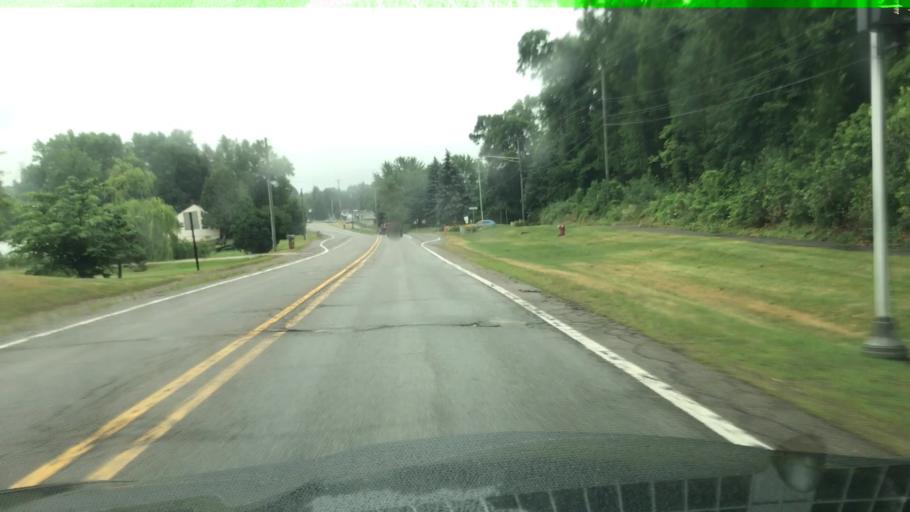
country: US
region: Michigan
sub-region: Oakland County
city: Auburn Hills
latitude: 42.7307
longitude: -83.2880
